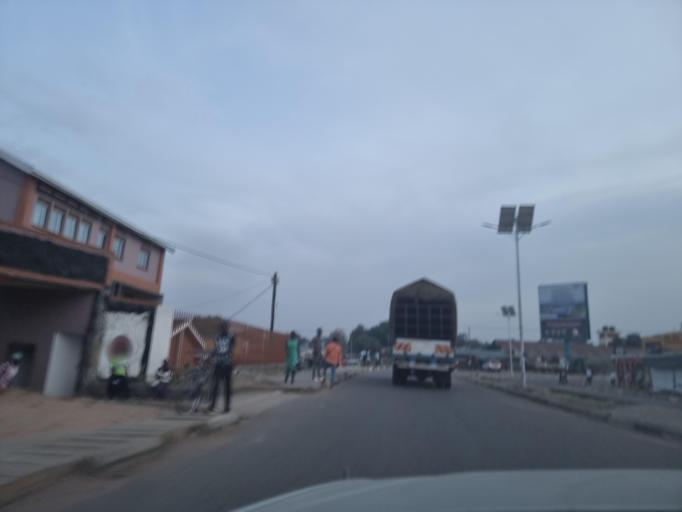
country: UG
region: Northern Region
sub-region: Arua District
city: Arua
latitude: 3.0222
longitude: 30.9127
